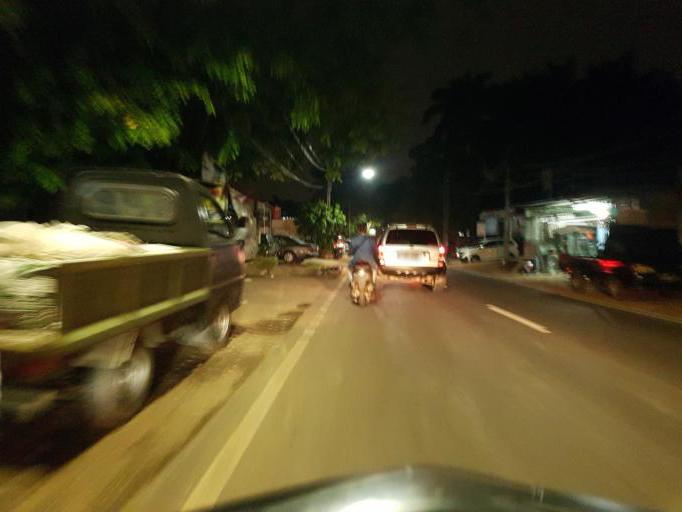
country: ID
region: West Java
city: Cileungsir
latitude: -6.3140
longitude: 106.9063
